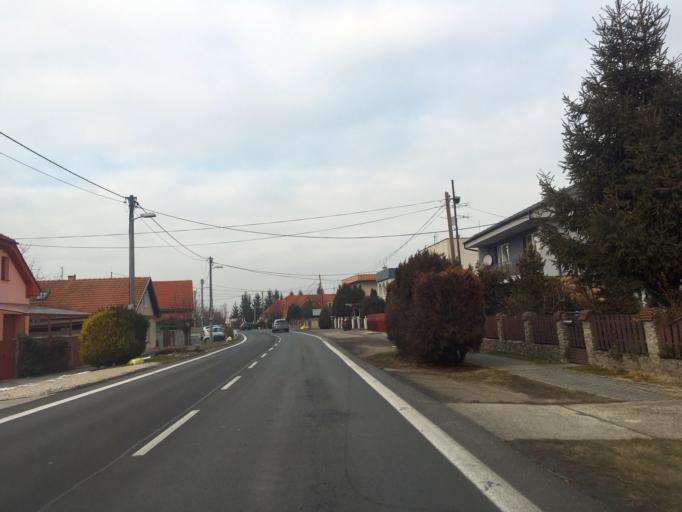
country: SK
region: Nitriansky
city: Sellye
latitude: 48.1661
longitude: 17.8837
